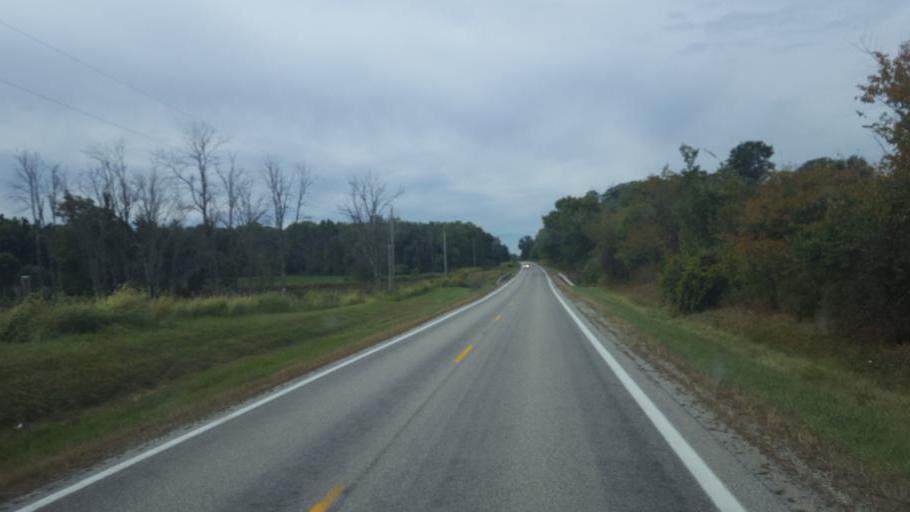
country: US
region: Ohio
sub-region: Knox County
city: Centerburg
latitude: 40.3633
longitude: -82.7568
